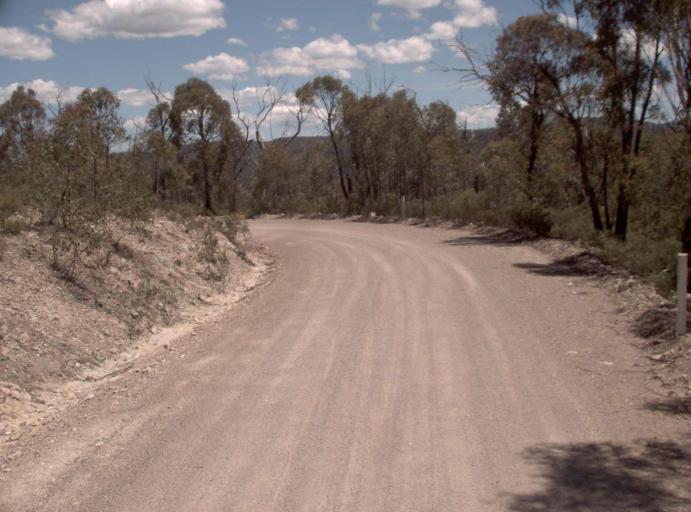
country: AU
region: New South Wales
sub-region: Snowy River
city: Jindabyne
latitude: -37.0734
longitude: 148.3255
